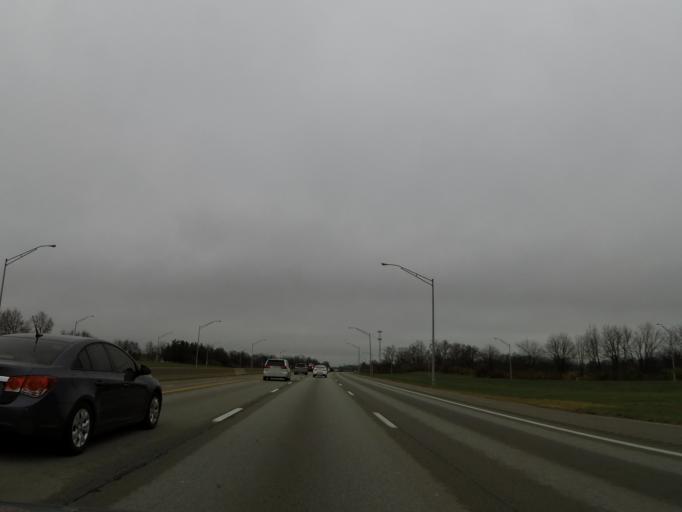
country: US
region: Kentucky
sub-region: Scott County
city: Georgetown
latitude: 38.1446
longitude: -84.5300
